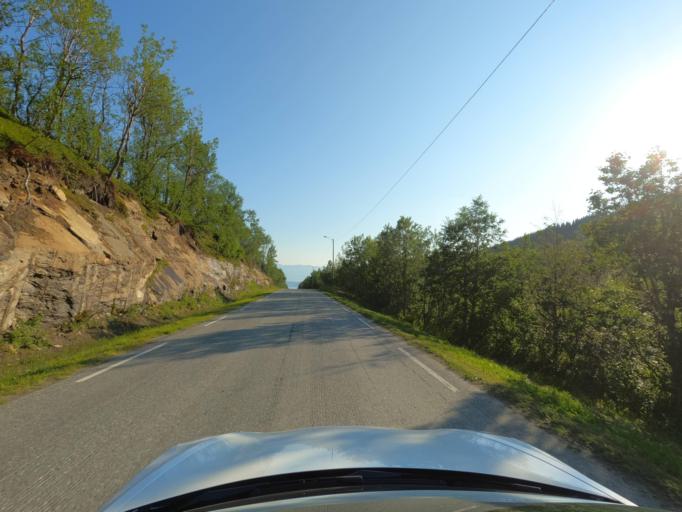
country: NO
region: Nordland
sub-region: Narvik
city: Bjerkvik
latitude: 68.5414
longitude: 17.4917
